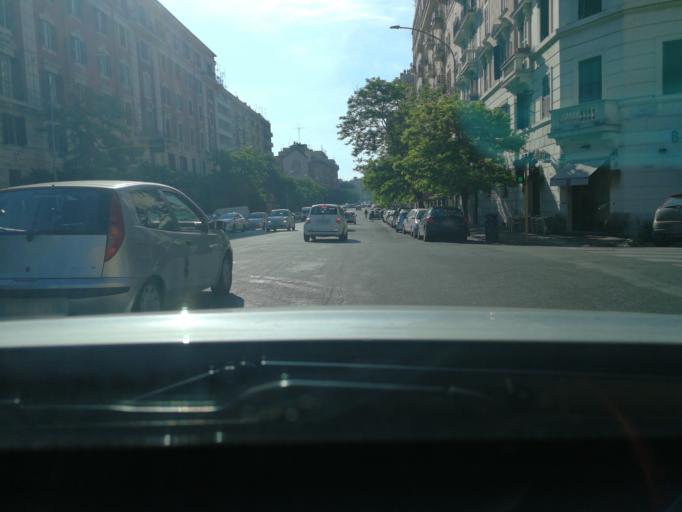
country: IT
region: Latium
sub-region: Citta metropolitana di Roma Capitale
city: Rome
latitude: 41.8851
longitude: 12.5126
